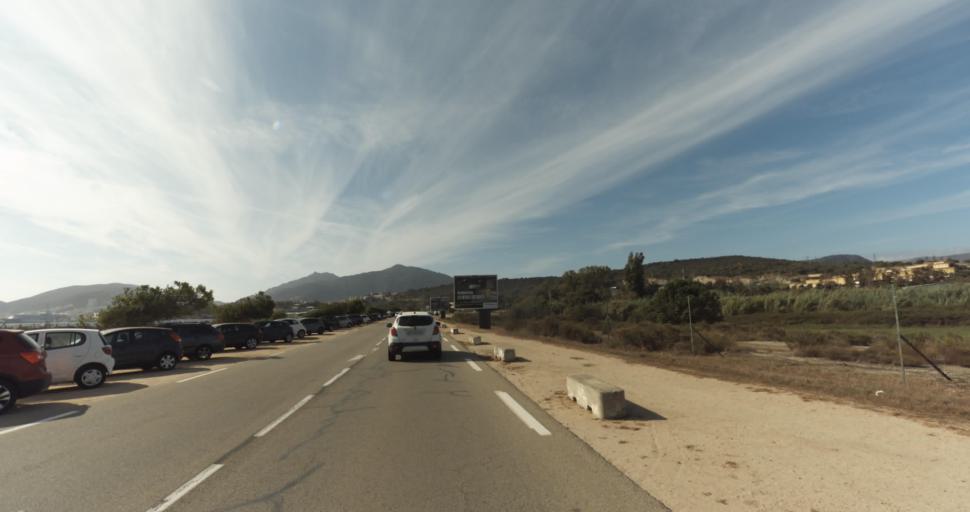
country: FR
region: Corsica
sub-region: Departement de la Corse-du-Sud
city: Ajaccio
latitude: 41.9247
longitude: 8.7826
